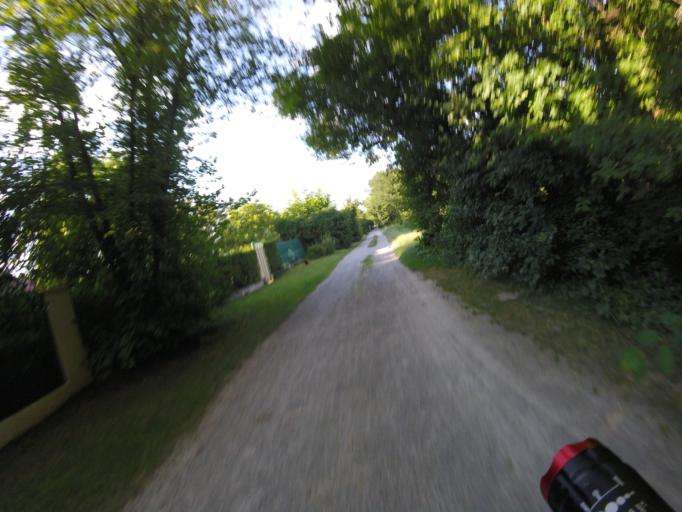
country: AT
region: Lower Austria
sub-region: Politischer Bezirk Modling
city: Munchendorf
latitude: 48.0217
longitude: 16.3726
